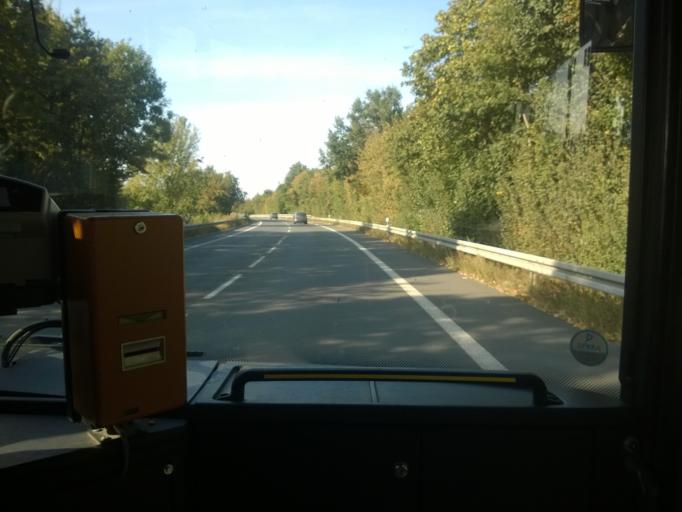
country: DE
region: North Rhine-Westphalia
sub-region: Regierungsbezirk Munster
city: Sudlohn
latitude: 51.8988
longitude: 6.8575
